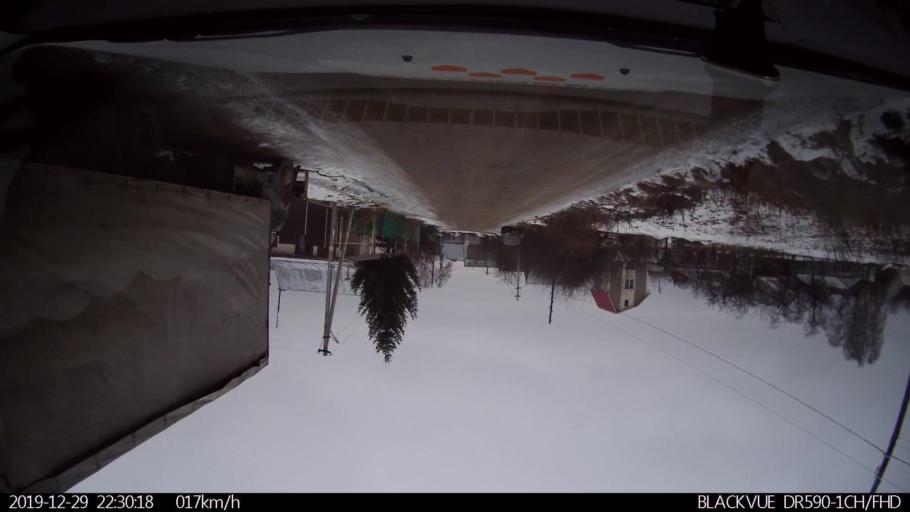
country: RU
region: Nizjnij Novgorod
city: Afonino
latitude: 56.2062
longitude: 43.9861
